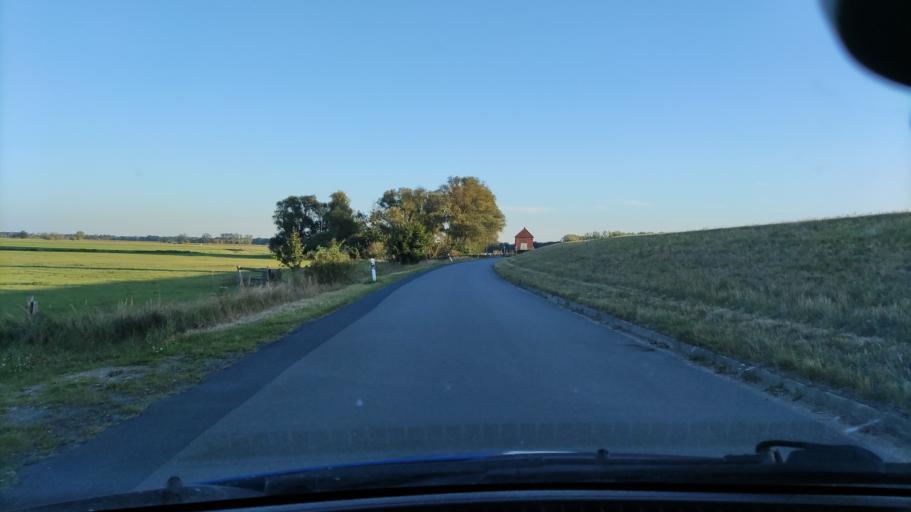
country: DE
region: Lower Saxony
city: Hitzacker
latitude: 53.1275
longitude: 11.0635
